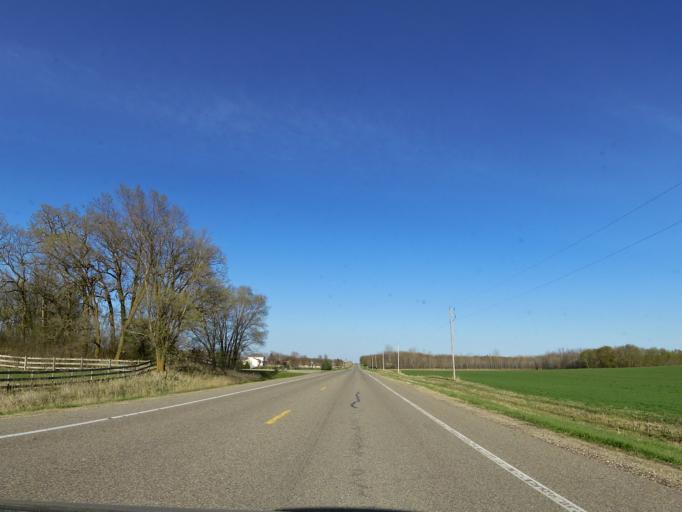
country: US
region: Minnesota
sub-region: Dakota County
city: Lakeville
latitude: 44.5872
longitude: -93.2570
